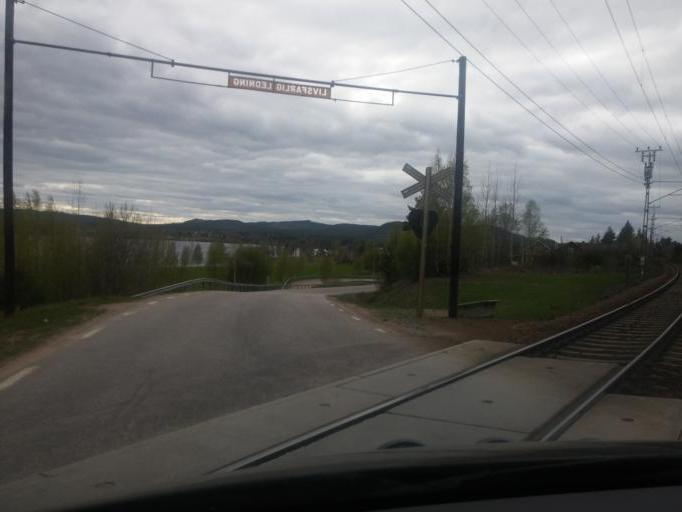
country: SE
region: Gaevleborg
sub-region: Ljusdals Kommun
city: Ljusdal
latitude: 61.8560
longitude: 16.0373
